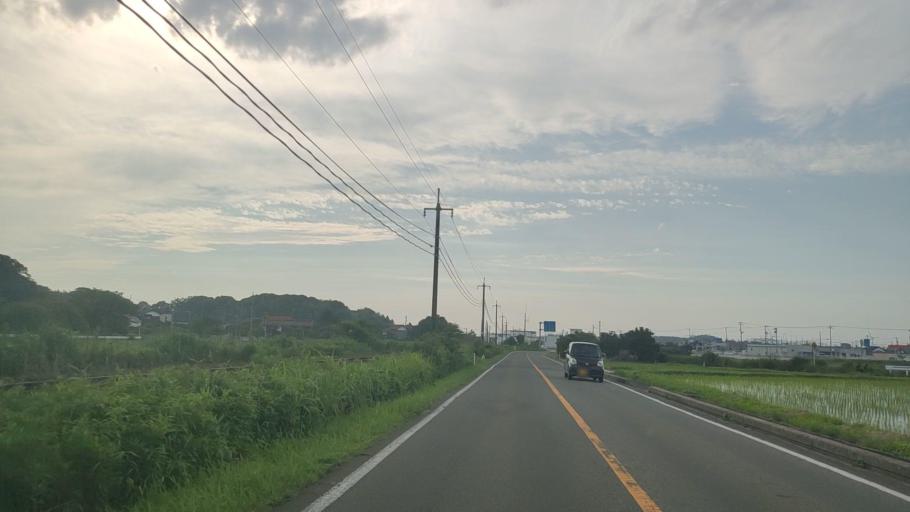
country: JP
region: Tottori
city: Kurayoshi
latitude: 35.4786
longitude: 133.8167
